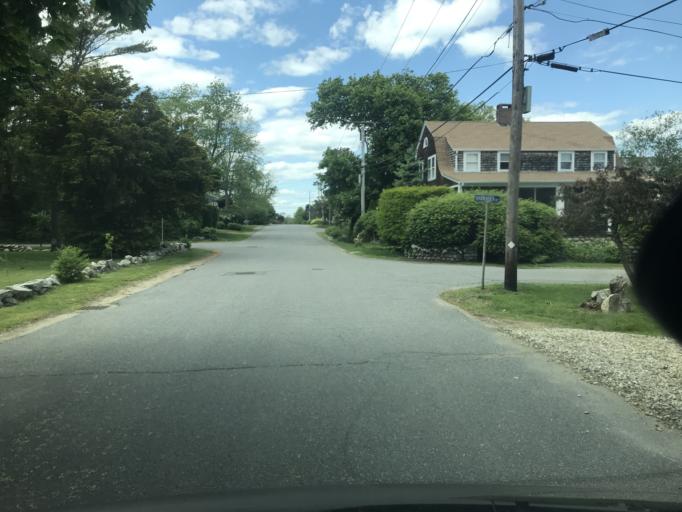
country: US
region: Massachusetts
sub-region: Essex County
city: Rockport
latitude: 42.6572
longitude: -70.6101
